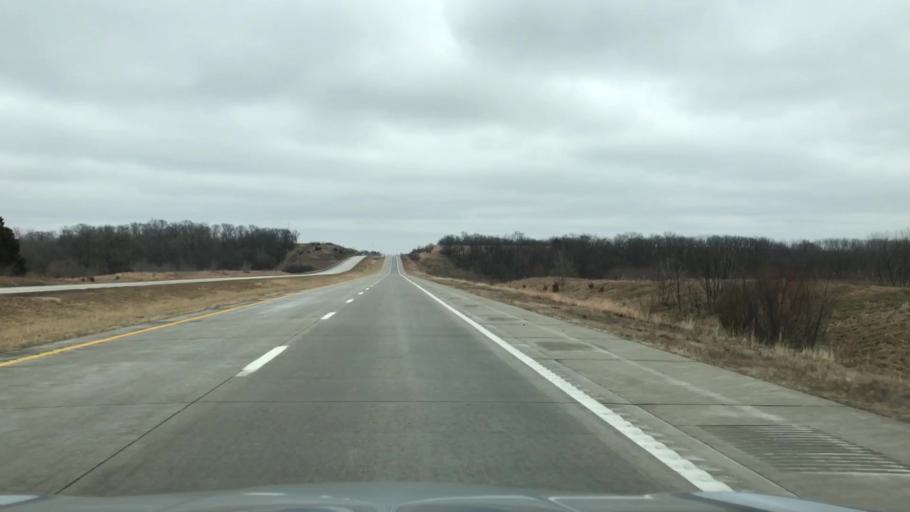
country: US
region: Missouri
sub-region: Caldwell County
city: Hamilton
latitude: 39.7350
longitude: -93.8266
